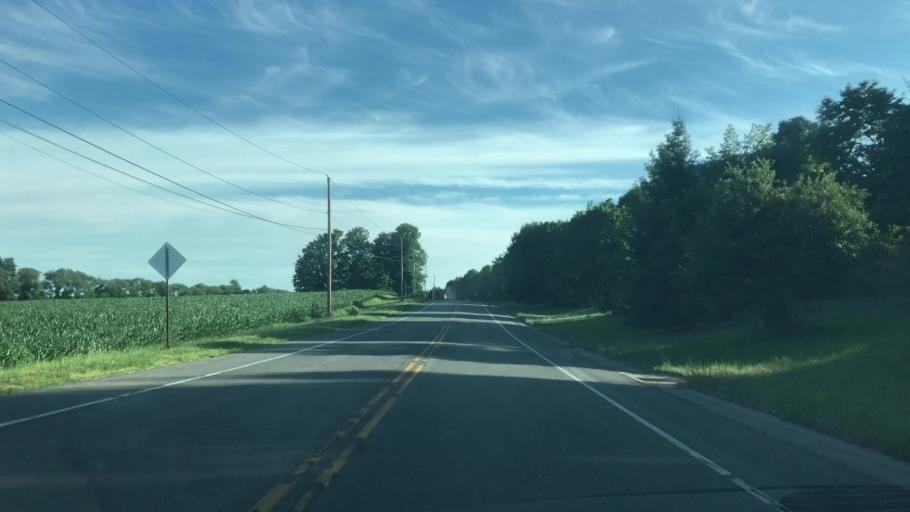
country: US
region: New York
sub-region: Ontario County
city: Victor
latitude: 43.0436
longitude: -77.3974
